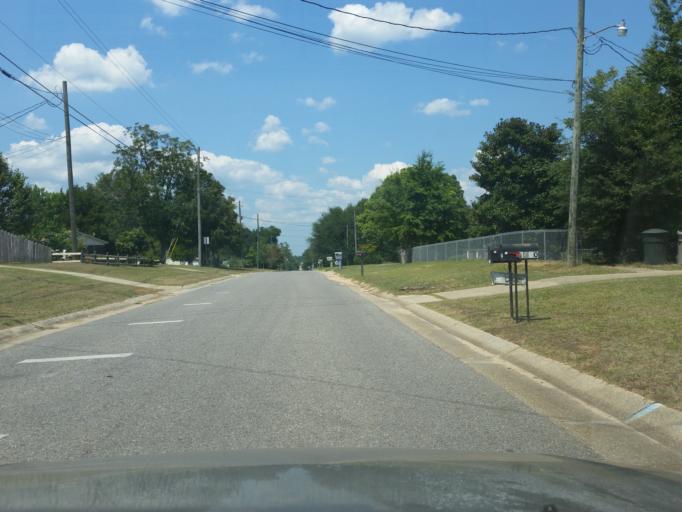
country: US
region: Florida
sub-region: Escambia County
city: Cantonment
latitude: 30.6428
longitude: -87.2918
